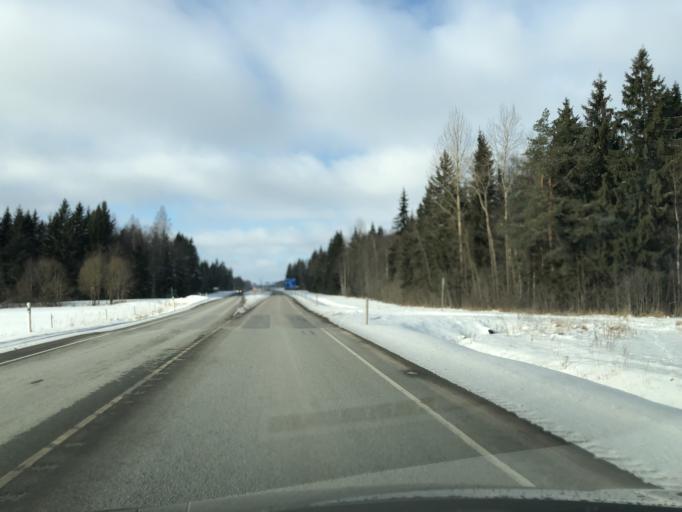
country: EE
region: Jaervamaa
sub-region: Paide linn
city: Paide
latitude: 58.8951
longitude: 25.6616
